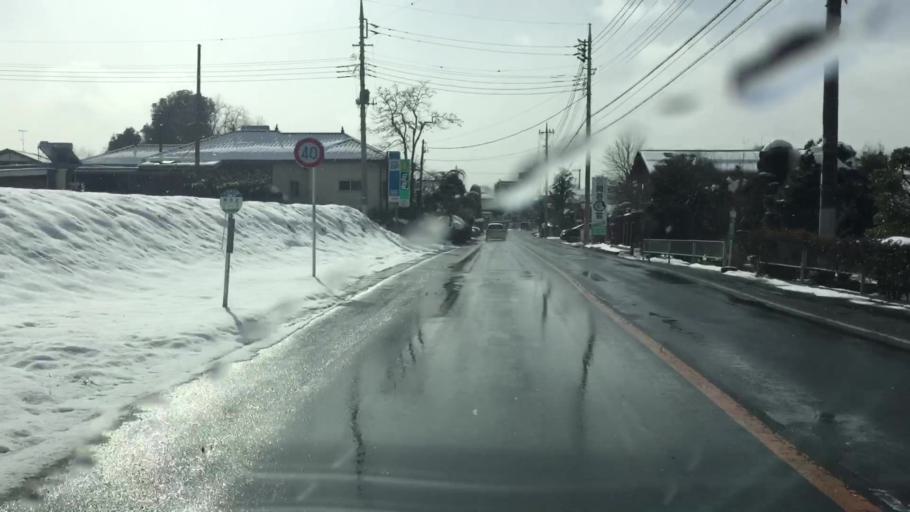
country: JP
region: Gunma
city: Numata
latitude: 36.6711
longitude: 139.0628
